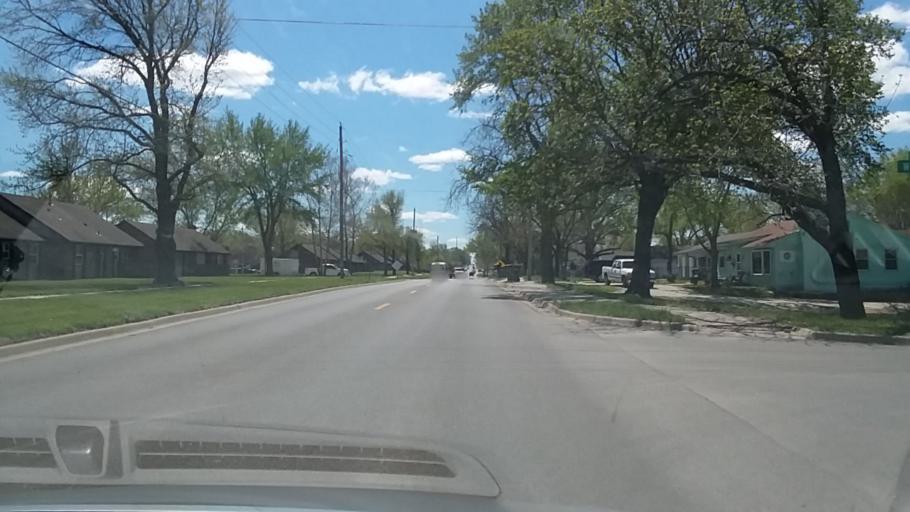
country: US
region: Kansas
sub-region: Douglas County
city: Lawrence
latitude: 38.9547
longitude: -95.2236
